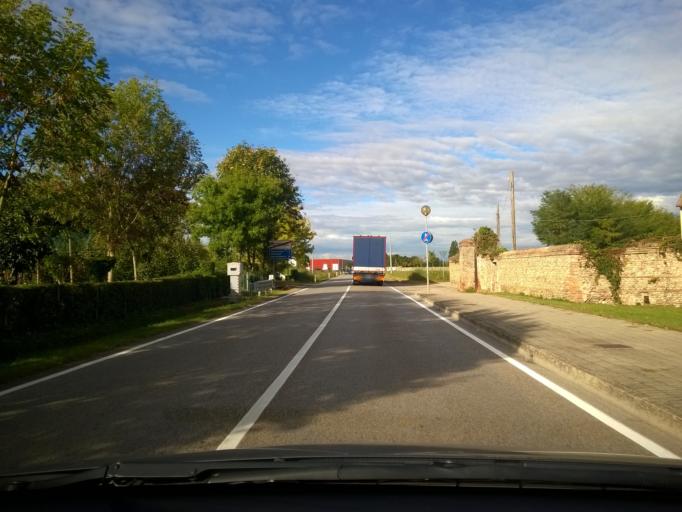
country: IT
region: Veneto
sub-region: Provincia di Treviso
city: Istrana
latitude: 45.6789
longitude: 12.0921
